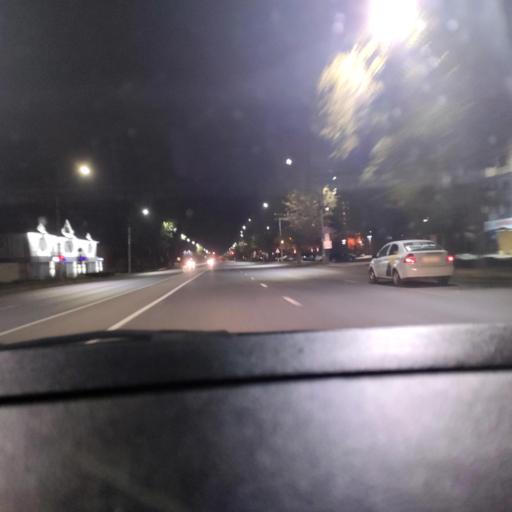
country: RU
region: Voronezj
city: Voronezh
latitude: 51.6752
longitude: 39.1686
